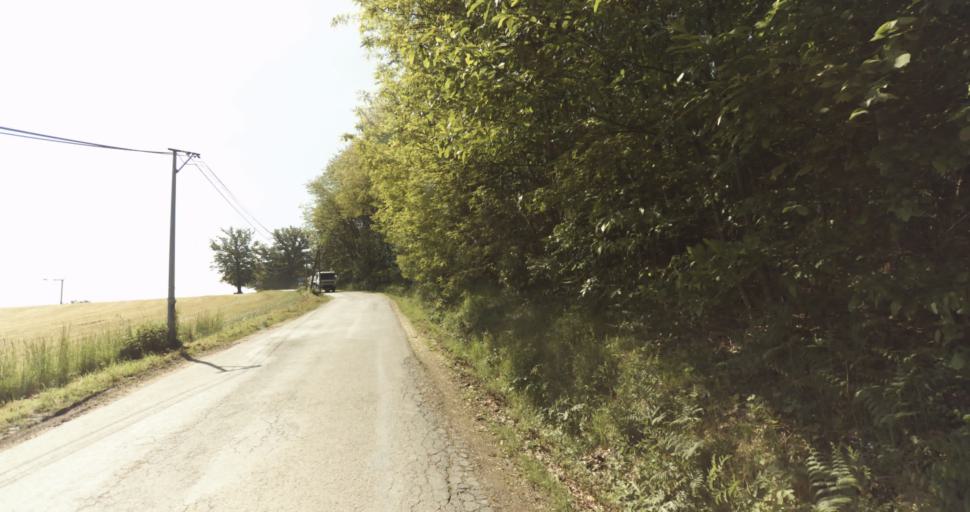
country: FR
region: Limousin
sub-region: Departement de la Haute-Vienne
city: Solignac
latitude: 45.7293
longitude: 1.2661
